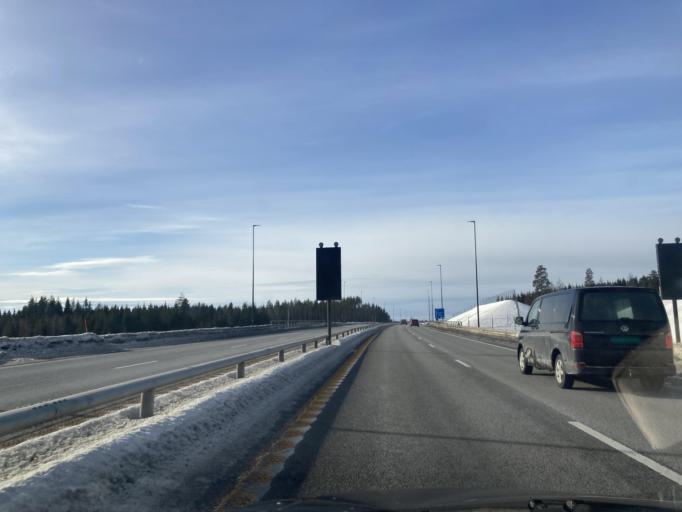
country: NO
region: Hedmark
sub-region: Loten
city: Loten
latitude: 60.8536
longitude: 11.3915
